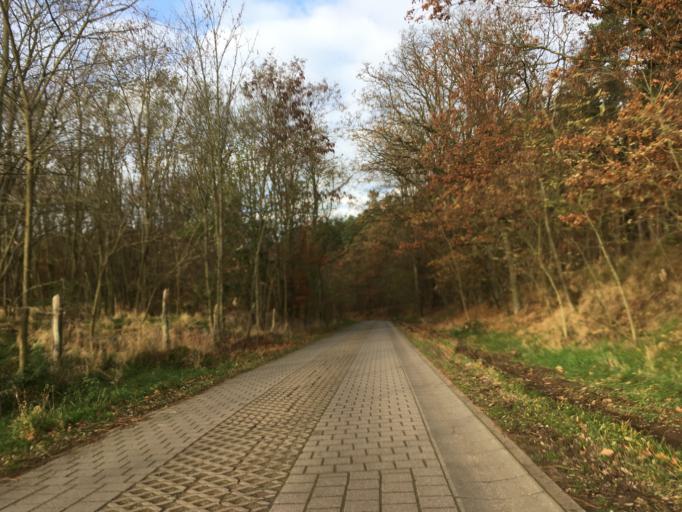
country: DE
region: Brandenburg
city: Muncheberg
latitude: 52.5619
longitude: 14.1304
